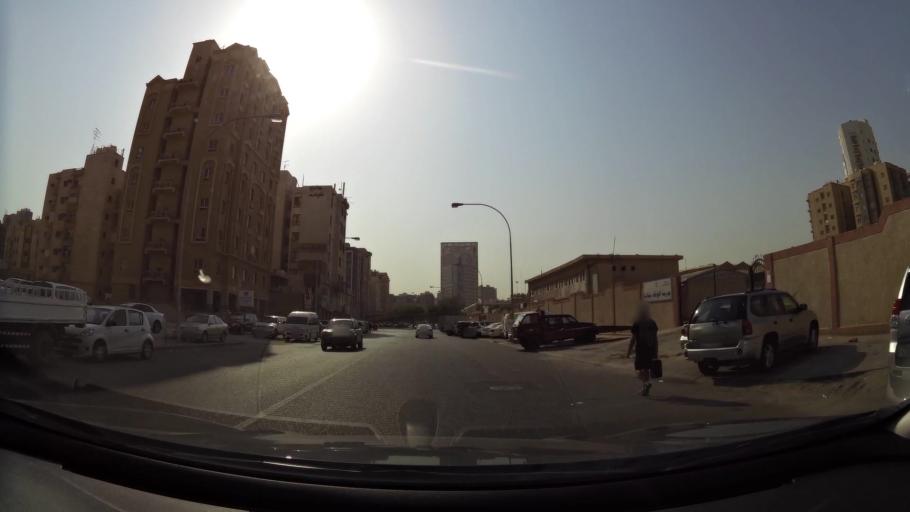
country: KW
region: Muhafazat Hawalli
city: Hawalli
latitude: 29.3266
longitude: 48.0131
